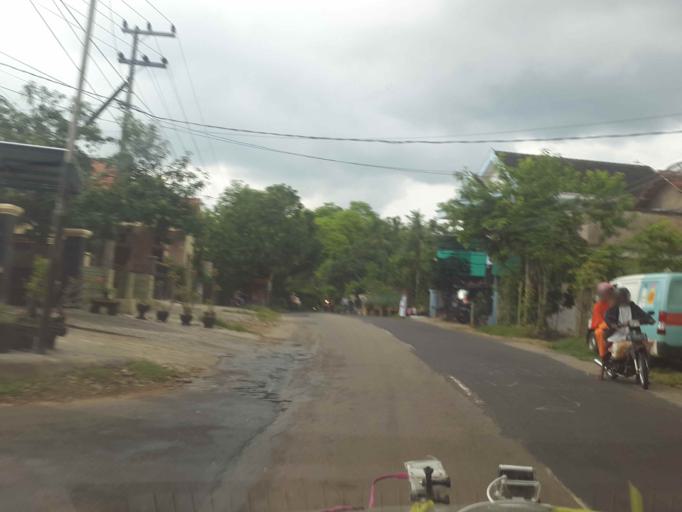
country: ID
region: East Java
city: Senmasen
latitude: -6.9918
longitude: 113.8655
